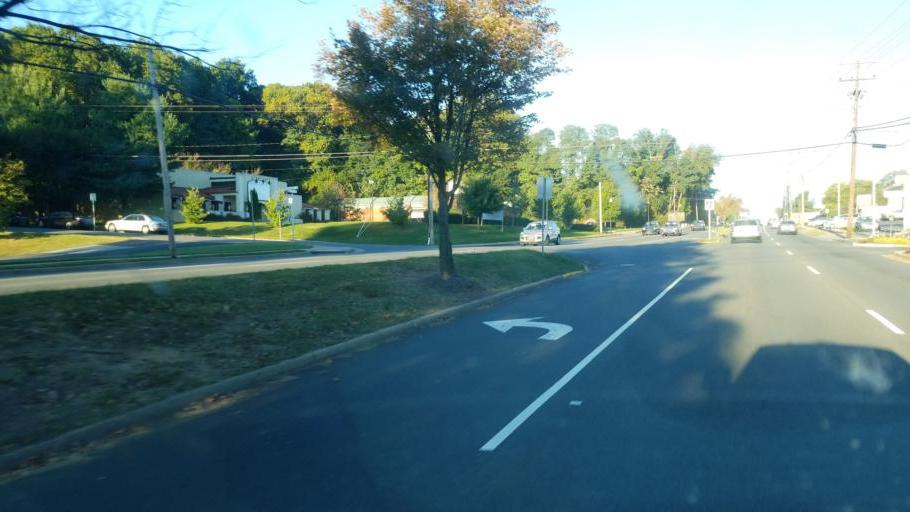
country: US
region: Virginia
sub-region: City of Fairfax
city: Fairfax
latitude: 38.8435
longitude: -77.2893
